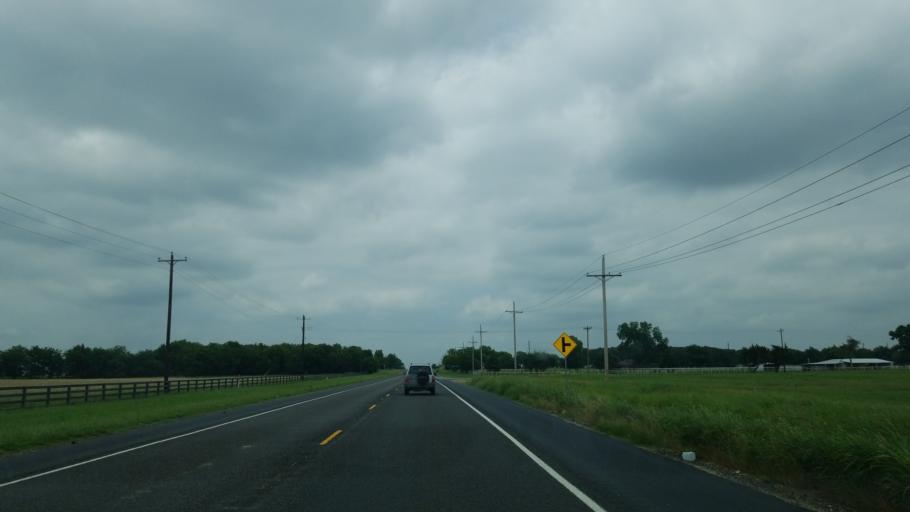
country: US
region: Texas
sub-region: Denton County
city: Pilot Point
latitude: 33.4369
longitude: -96.9289
